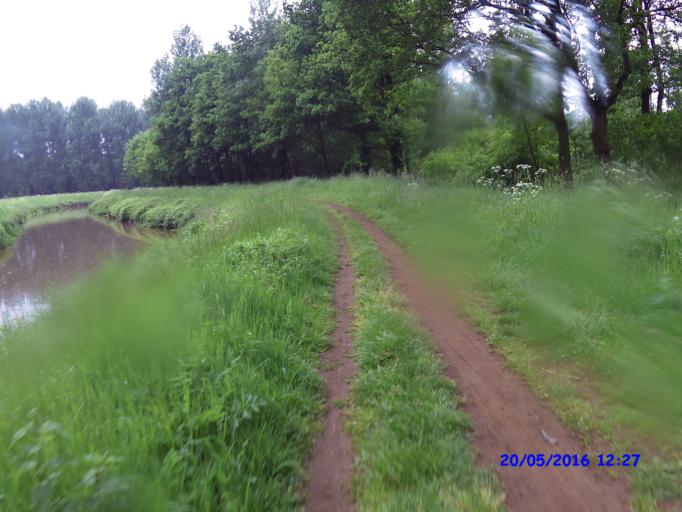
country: BE
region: Flanders
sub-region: Provincie Antwerpen
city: Hulshout
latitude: 51.0630
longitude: 4.7988
